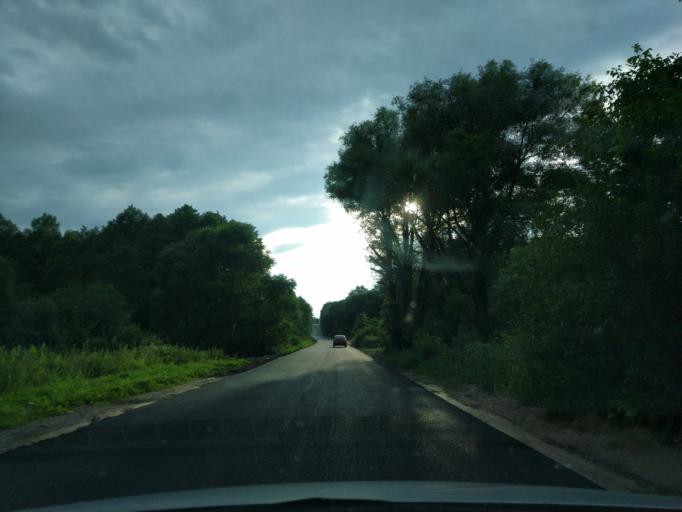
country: RU
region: Kaluga
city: Myatlevo
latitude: 54.8003
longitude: 35.7298
